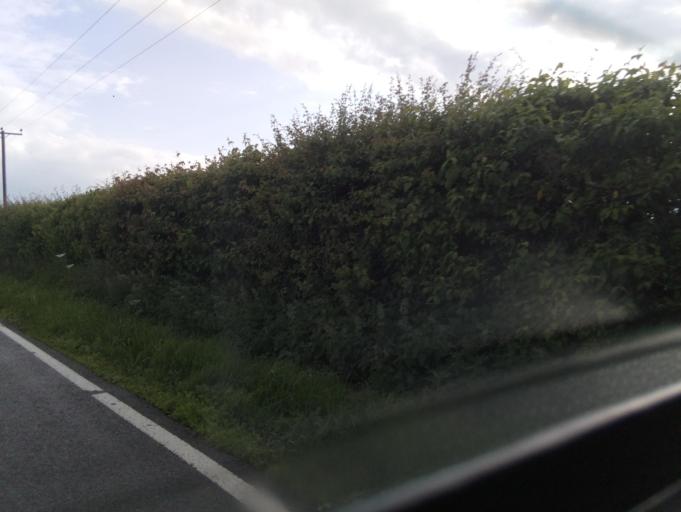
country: GB
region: England
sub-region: Lincolnshire
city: Great Gonerby
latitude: 53.0281
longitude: -0.6547
